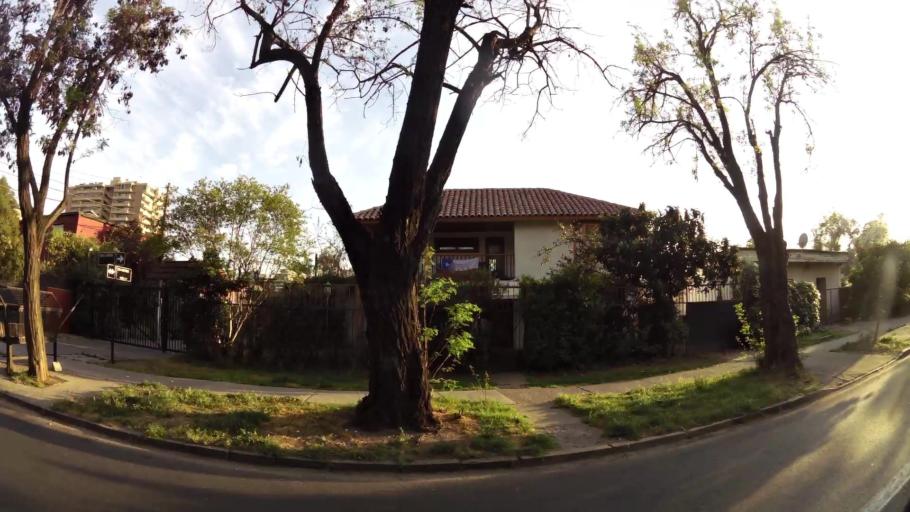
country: CL
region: Santiago Metropolitan
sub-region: Provincia de Santiago
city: Villa Presidente Frei, Nunoa, Santiago, Chile
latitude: -33.4599
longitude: -70.5752
